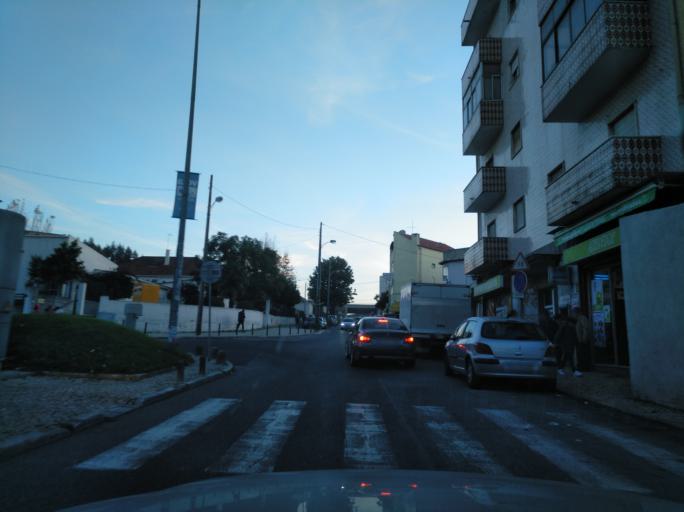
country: PT
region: Lisbon
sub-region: Odivelas
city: Olival do Basto
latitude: 38.7922
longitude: -9.1507
